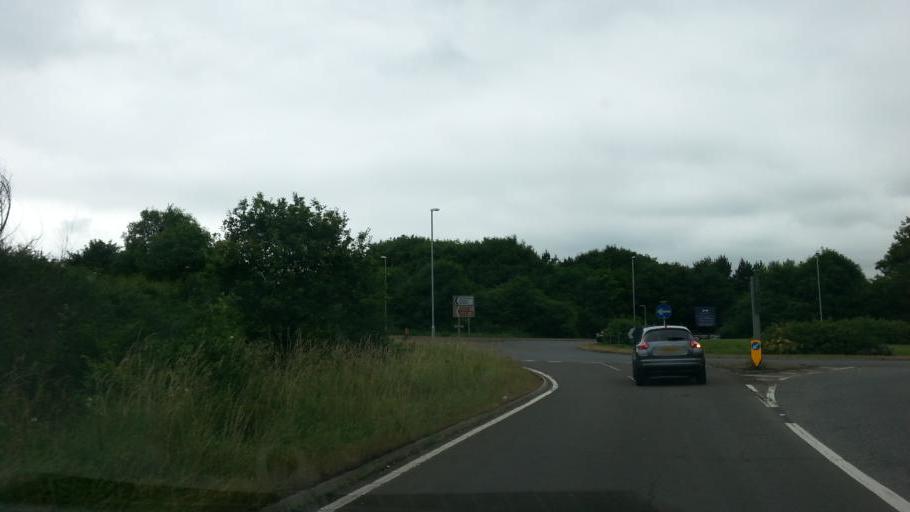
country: GB
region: England
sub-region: Northamptonshire
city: Geddington
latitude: 52.4216
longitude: -0.6974
